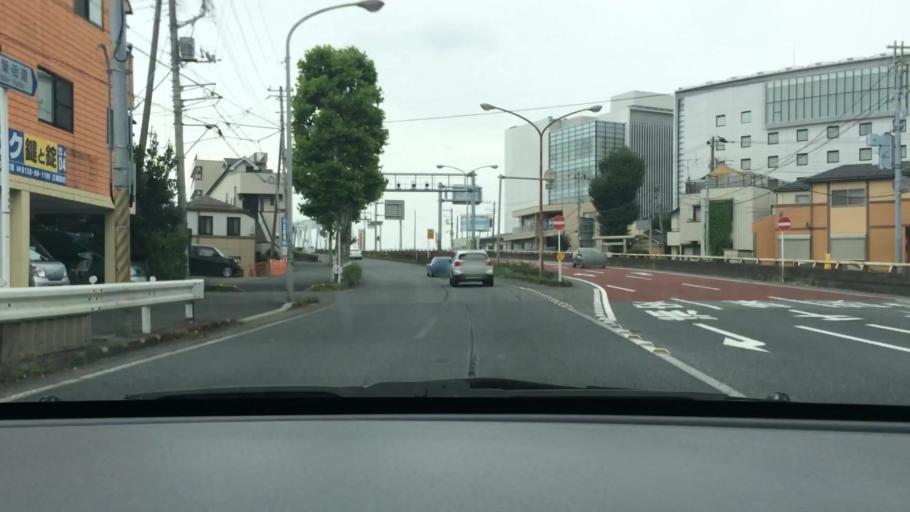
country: JP
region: Chiba
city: Matsudo
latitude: 35.7330
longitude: 139.9021
